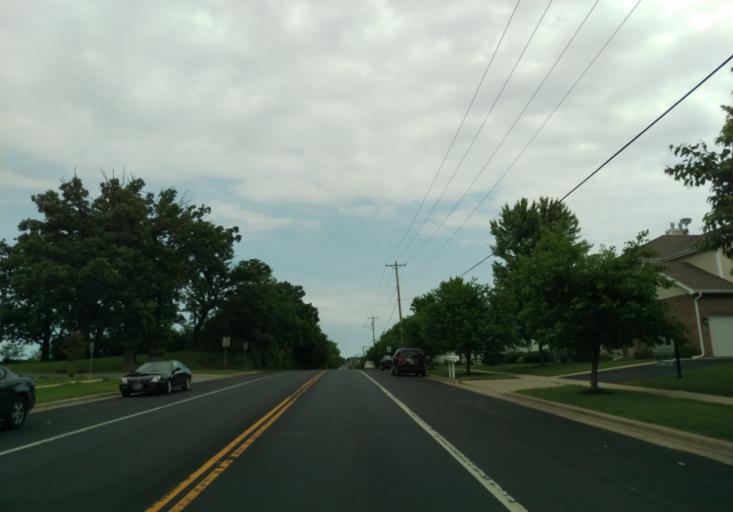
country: US
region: Wisconsin
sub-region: Dane County
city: Verona
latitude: 43.0053
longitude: -89.4990
